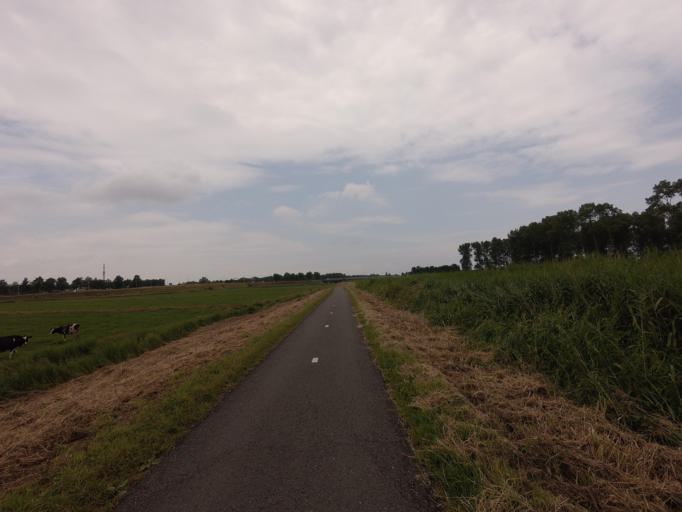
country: NL
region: North Holland
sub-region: Gemeente Purmerend
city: Purmerend
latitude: 52.4832
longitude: 4.9538
